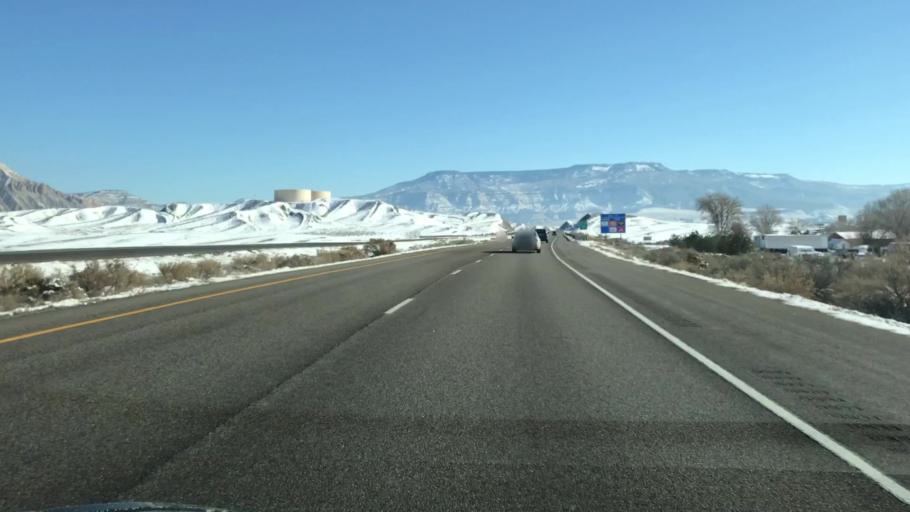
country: US
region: Colorado
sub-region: Mesa County
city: Clifton
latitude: 39.1046
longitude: -108.4712
